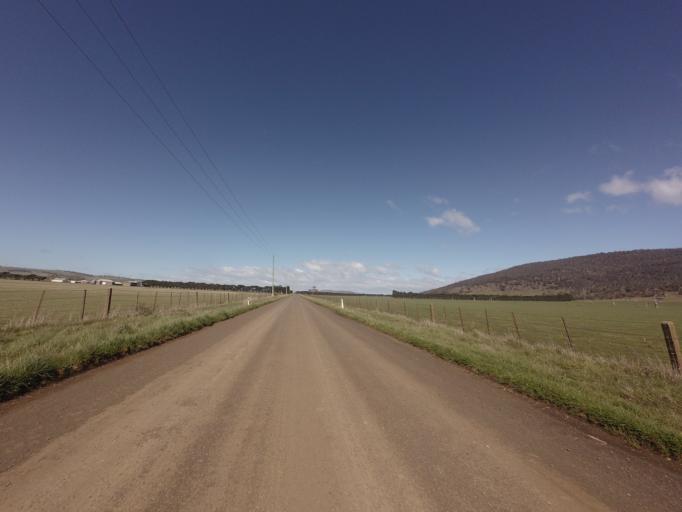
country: AU
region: Tasmania
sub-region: Northern Midlands
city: Evandale
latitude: -41.9580
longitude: 147.4372
